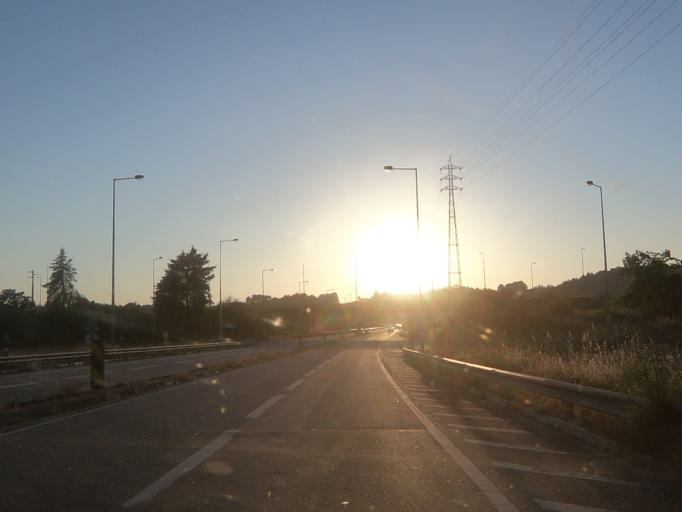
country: PT
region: Viseu
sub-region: Viseu
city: Rio de Loba
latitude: 40.6804
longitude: -7.8811
